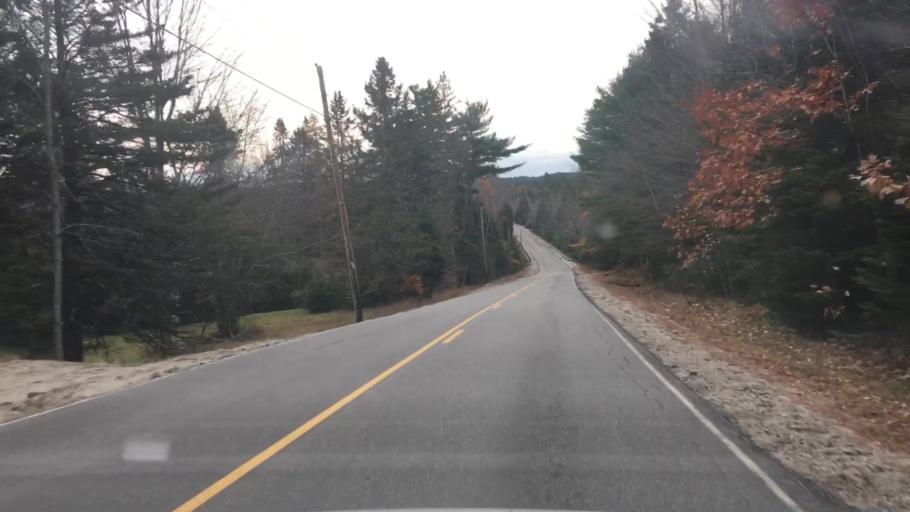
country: US
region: Maine
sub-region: Hancock County
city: Penobscot
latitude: 44.4283
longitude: -68.6252
